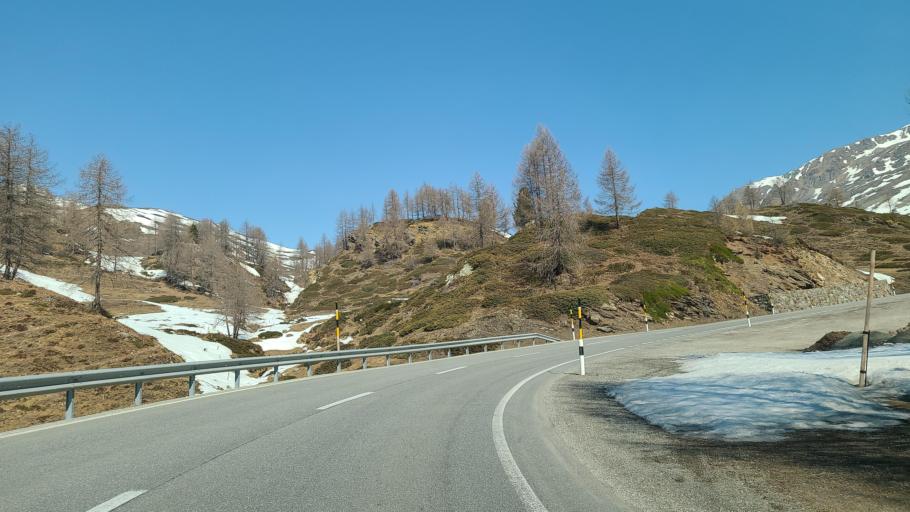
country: CH
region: Grisons
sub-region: Bernina District
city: Poschiavo
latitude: 46.4081
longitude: 10.0501
